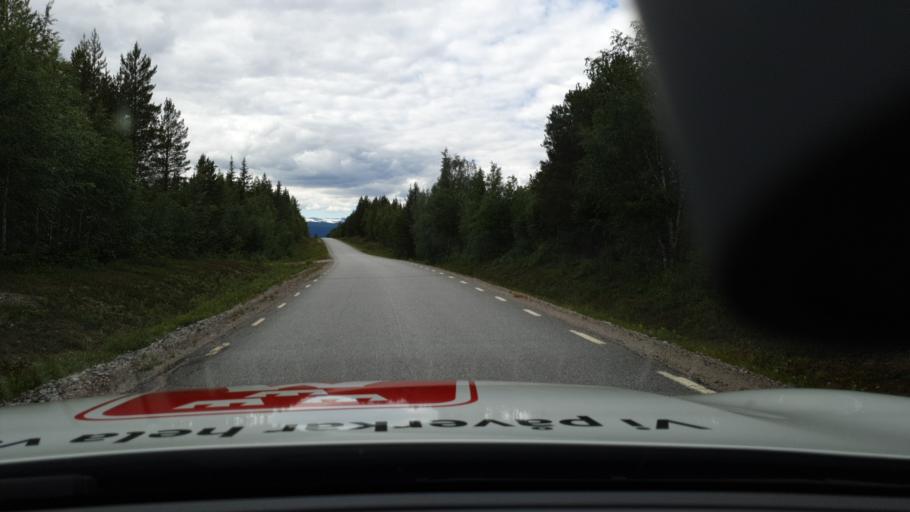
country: SE
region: Norrbotten
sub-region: Arjeplogs Kommun
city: Arjeplog
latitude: 66.8841
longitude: 18.1275
